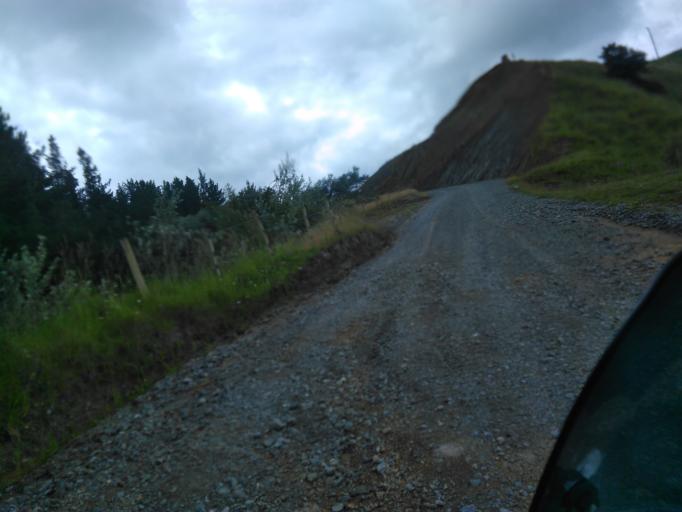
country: NZ
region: Gisborne
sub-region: Gisborne District
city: Gisborne
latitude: -38.0725
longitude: 178.0446
